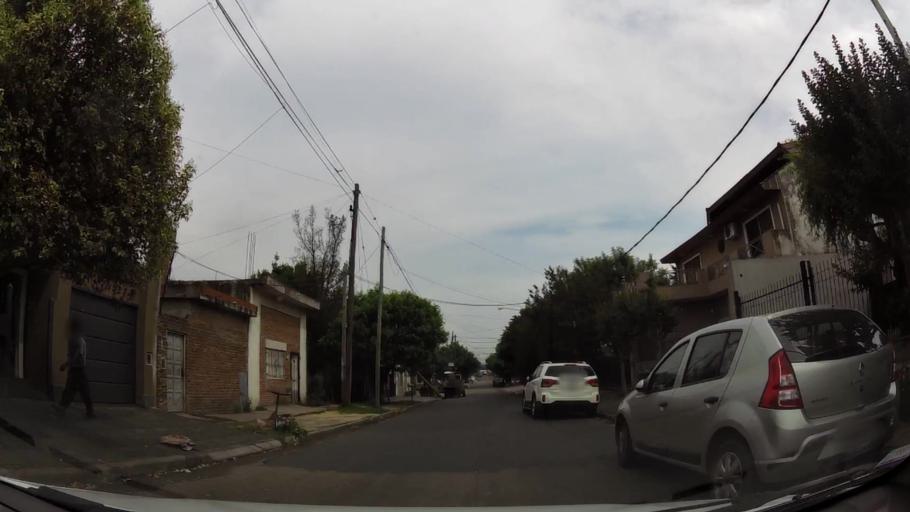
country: AR
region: Buenos Aires
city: San Justo
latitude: -34.6966
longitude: -58.5304
